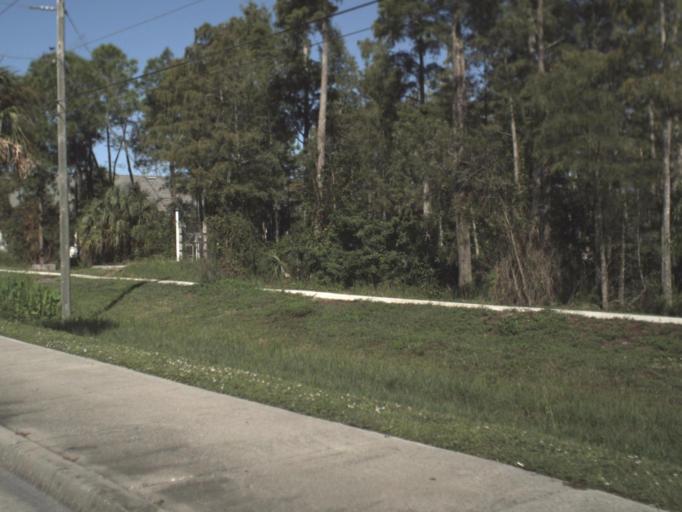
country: US
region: Florida
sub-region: Collier County
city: Vineyards
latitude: 26.2117
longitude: -81.7472
